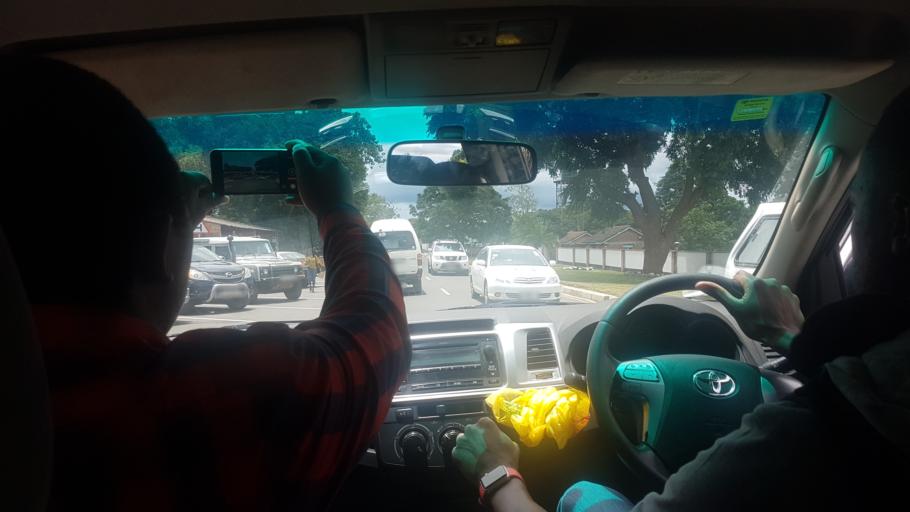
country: ZM
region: Lusaka
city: Lusaka
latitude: -15.4250
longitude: 28.3074
